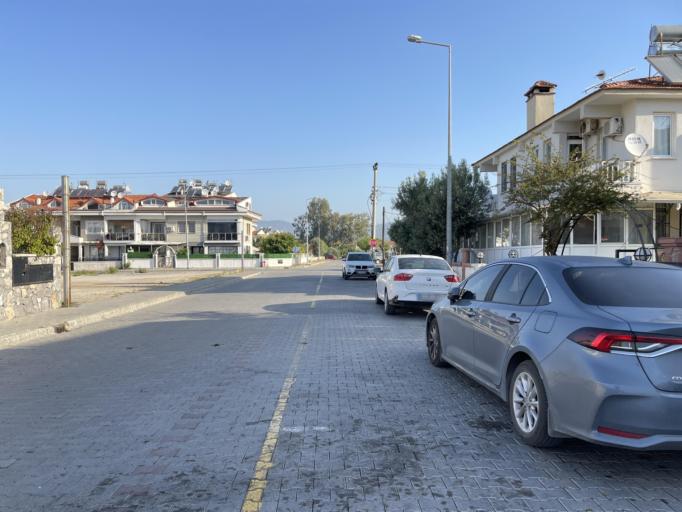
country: TR
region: Mugla
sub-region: Fethiye
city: Fethiye
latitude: 36.6579
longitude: 29.1229
